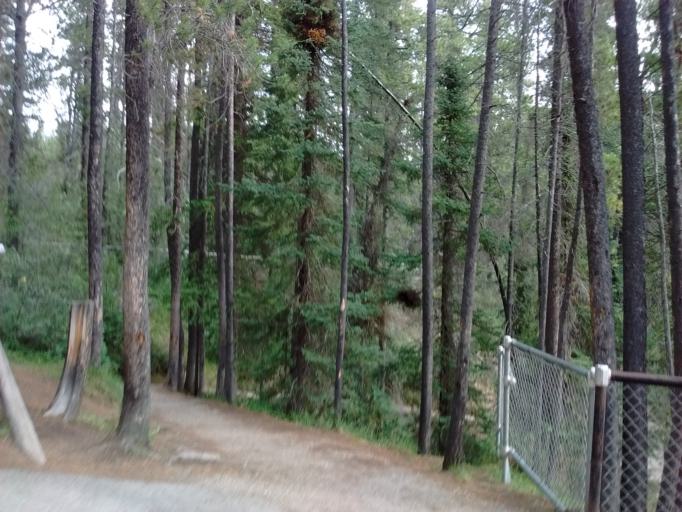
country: CA
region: Alberta
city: Jasper Park Lodge
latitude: 52.5320
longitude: -117.6455
